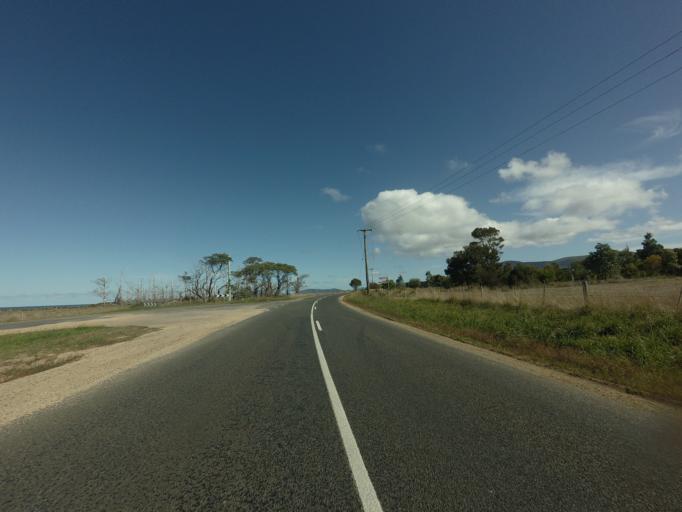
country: AU
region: Tasmania
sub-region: Break O'Day
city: St Helens
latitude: -41.7496
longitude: 148.2777
